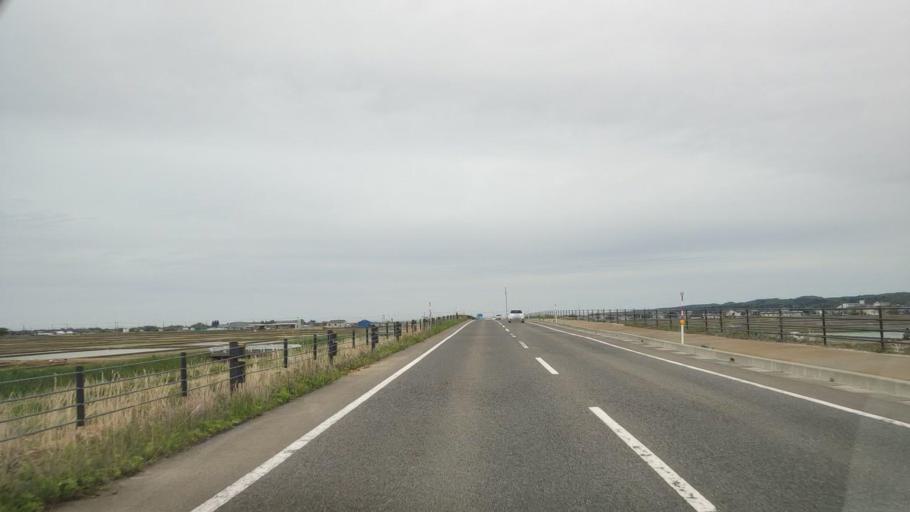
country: JP
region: Niigata
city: Shirone
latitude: 37.7457
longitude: 139.0836
